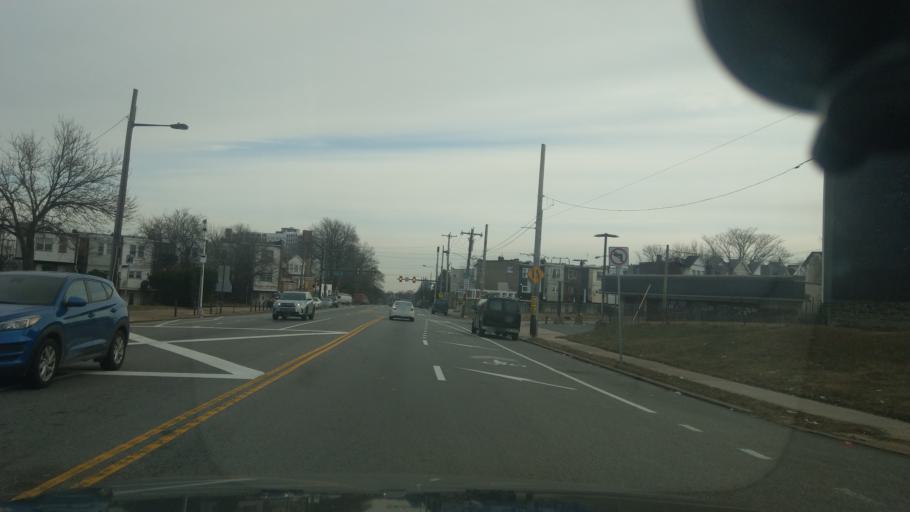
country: US
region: Pennsylvania
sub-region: Montgomery County
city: Wyncote
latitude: 40.0515
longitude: -75.1500
